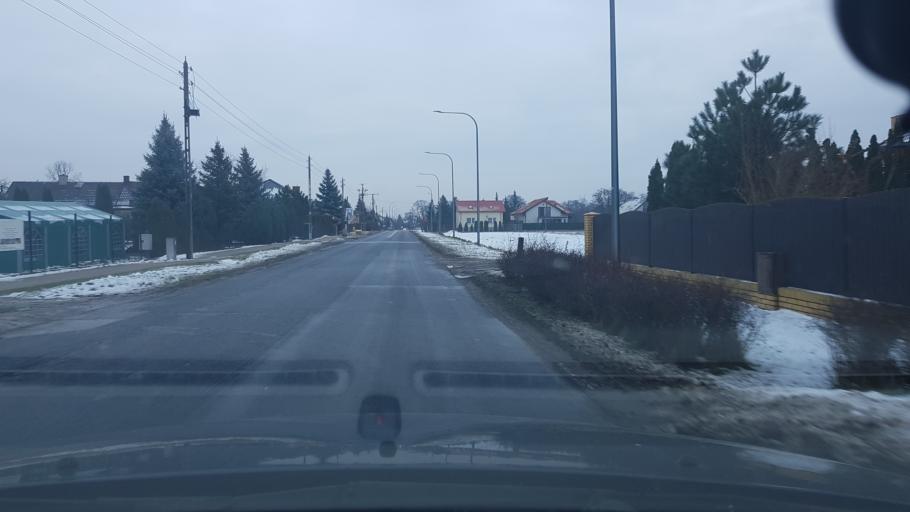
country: PL
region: Masovian Voivodeship
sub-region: Warszawa
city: Targowek
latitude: 52.3072
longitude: 21.0325
